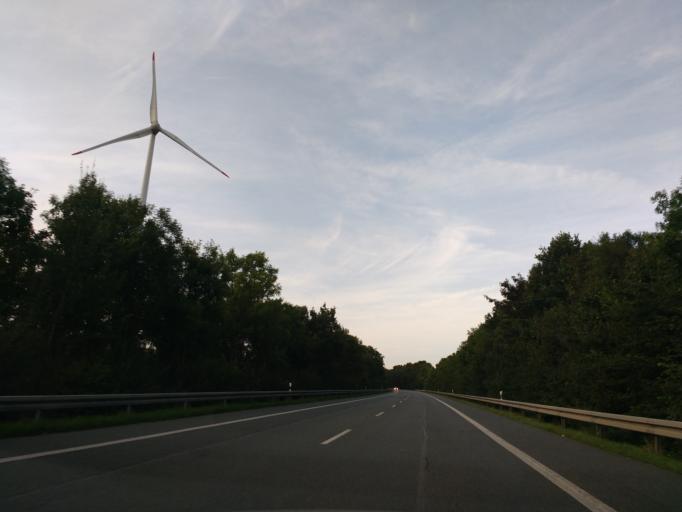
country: DE
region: North Rhine-Westphalia
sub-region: Regierungsbezirk Detmold
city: Wunnenberg
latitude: 51.5462
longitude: 8.7127
